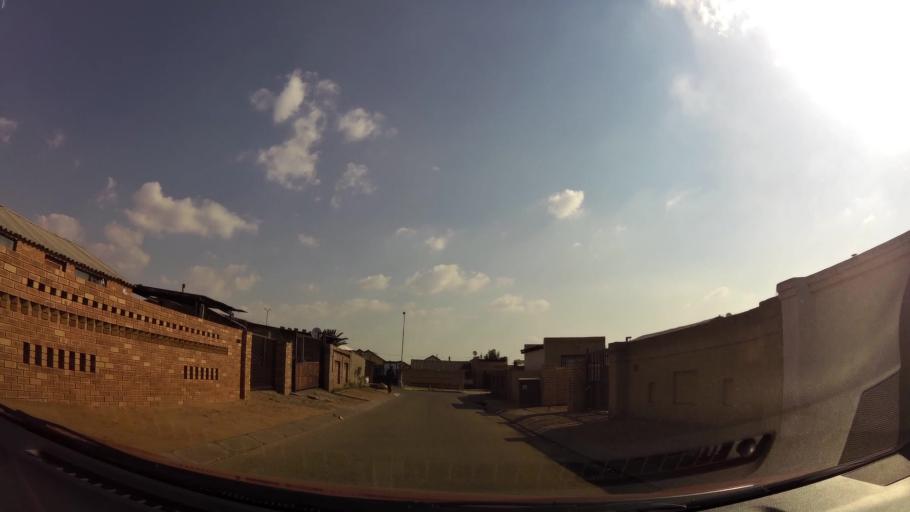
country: ZA
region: Gauteng
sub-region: City of Johannesburg Metropolitan Municipality
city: Soweto
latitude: -26.2391
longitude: 27.9482
